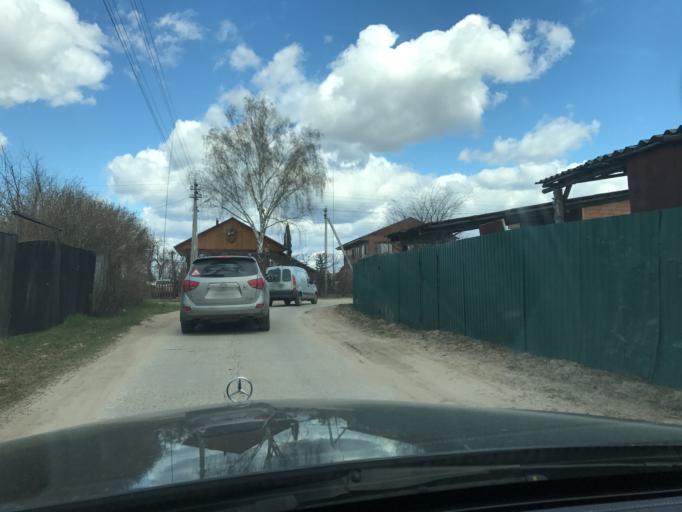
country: RU
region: Vladimir
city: Pokrov
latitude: 55.8534
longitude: 39.1959
